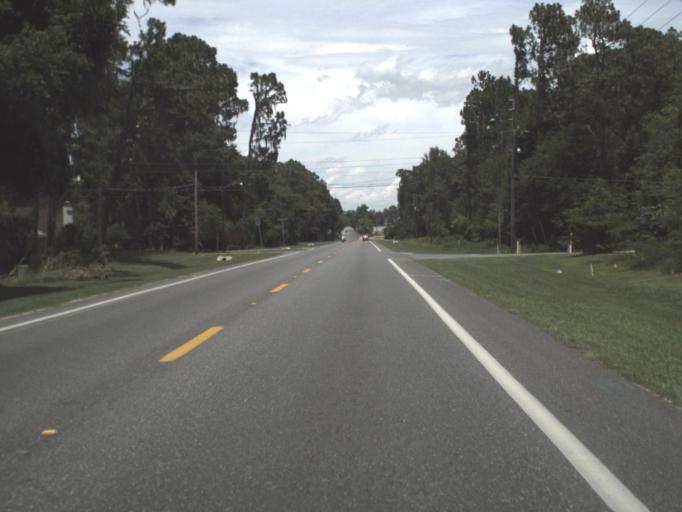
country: US
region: Florida
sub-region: Suwannee County
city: Live Oak
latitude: 30.2859
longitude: -83.0008
